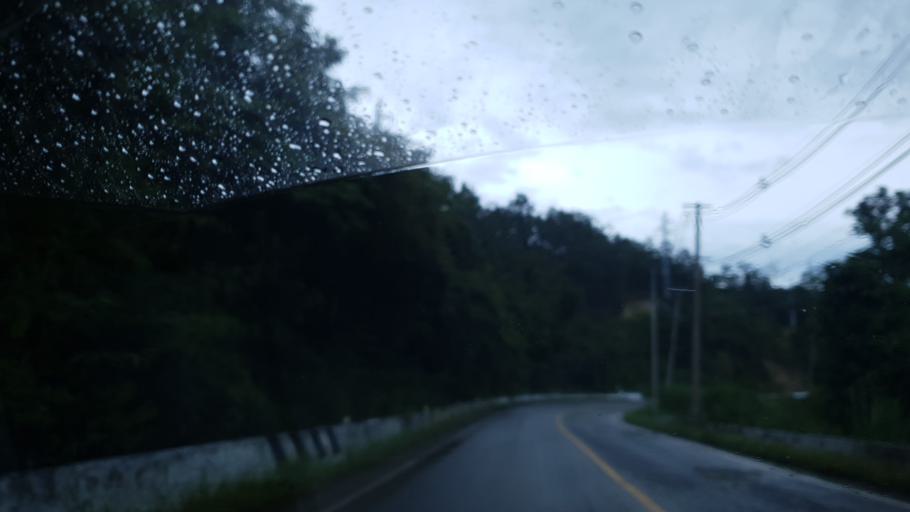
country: TH
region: Mae Hong Son
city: Ban Huai I Huak
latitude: 18.1407
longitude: 98.2019
